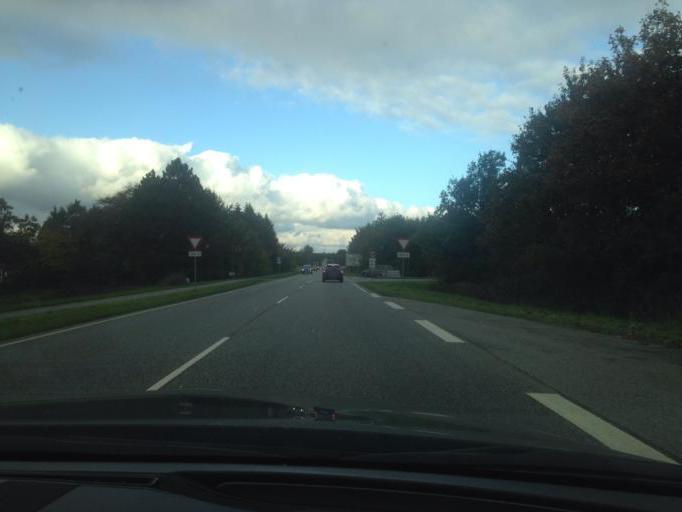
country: DK
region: South Denmark
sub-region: Kolding Kommune
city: Kolding
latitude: 55.5417
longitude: 9.4750
